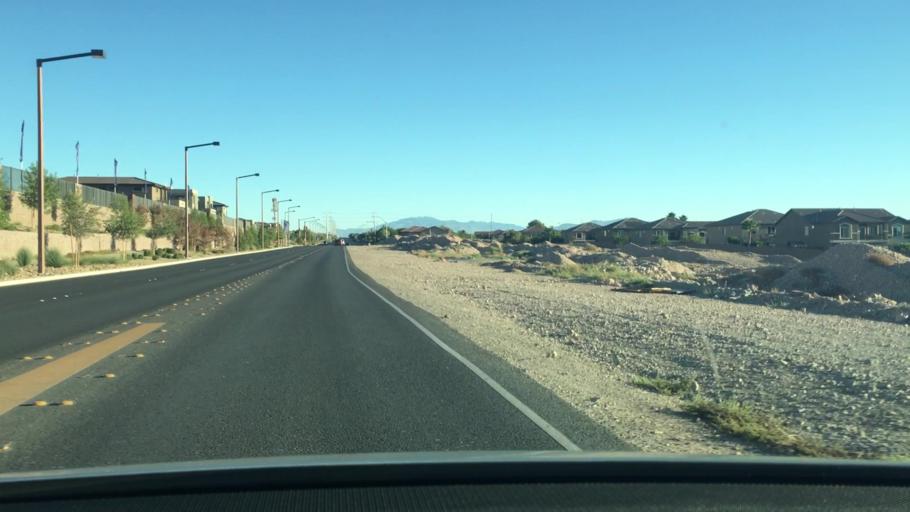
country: US
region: Nevada
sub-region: Clark County
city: Summerlin South
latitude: 36.0747
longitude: -115.3157
